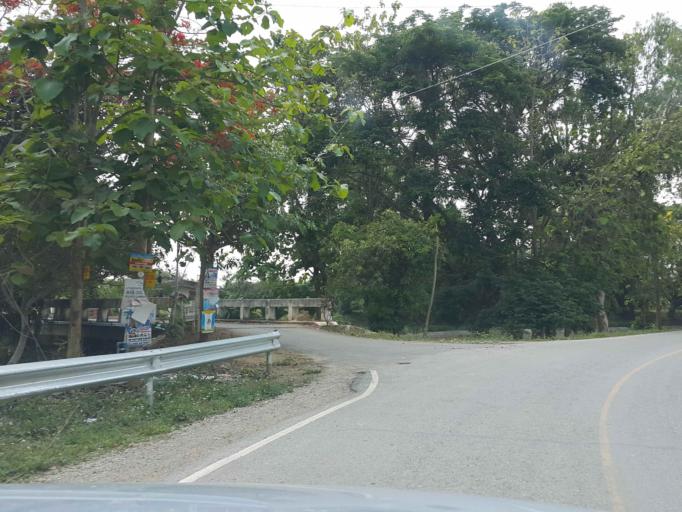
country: TH
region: Chiang Mai
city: Saraphi
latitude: 18.6871
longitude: 98.9920
